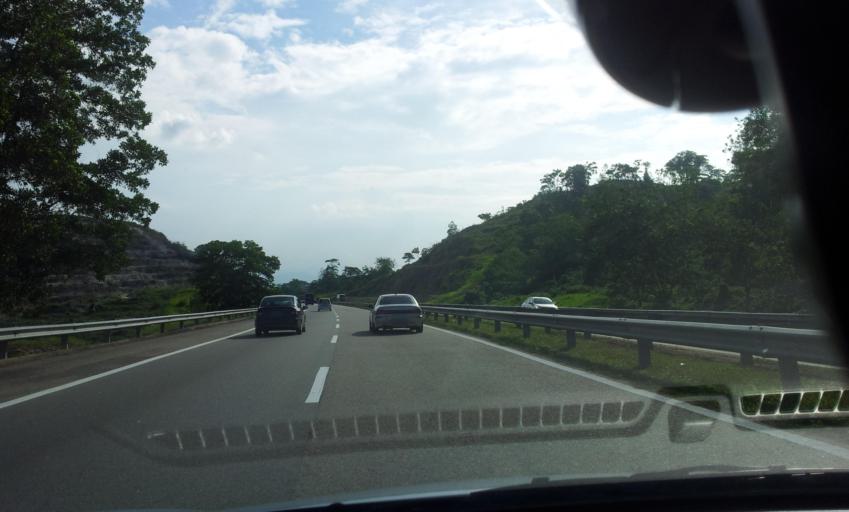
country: MY
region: Pahang
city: Mentekab
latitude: 3.5119
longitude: 102.1308
